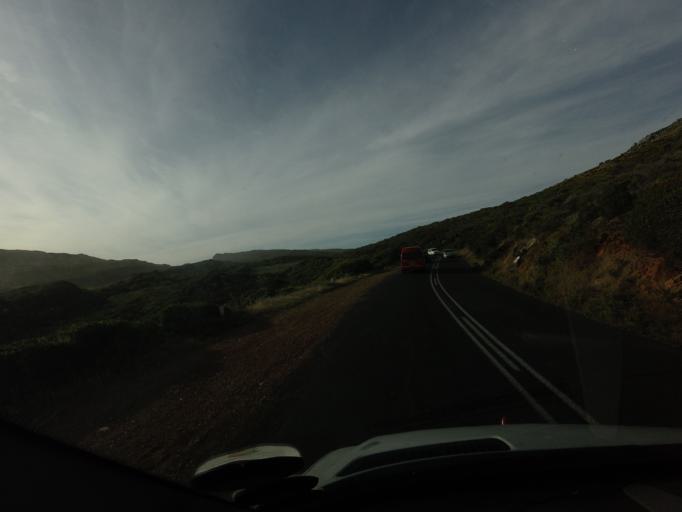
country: ZA
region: Western Cape
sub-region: City of Cape Town
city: Constantia
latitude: -34.1707
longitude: 18.3473
